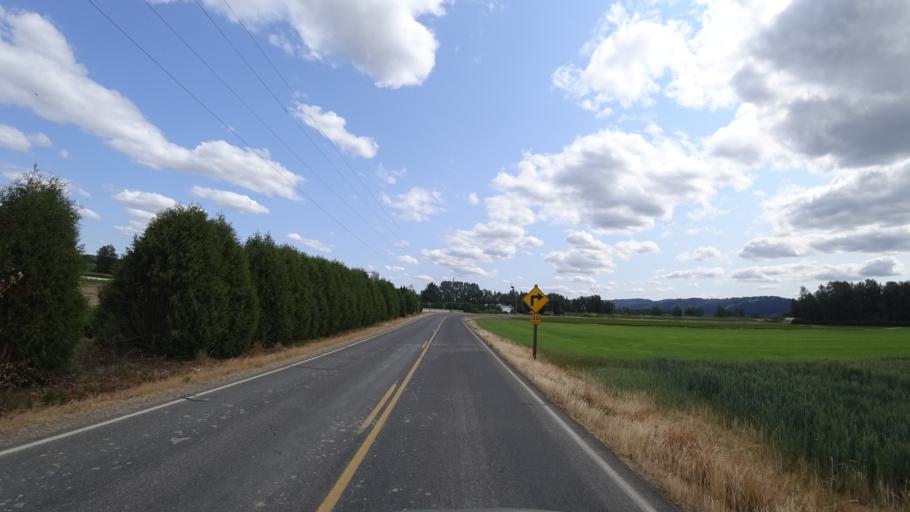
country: US
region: Washington
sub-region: Clark County
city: Felida
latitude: 45.6488
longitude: -122.7770
